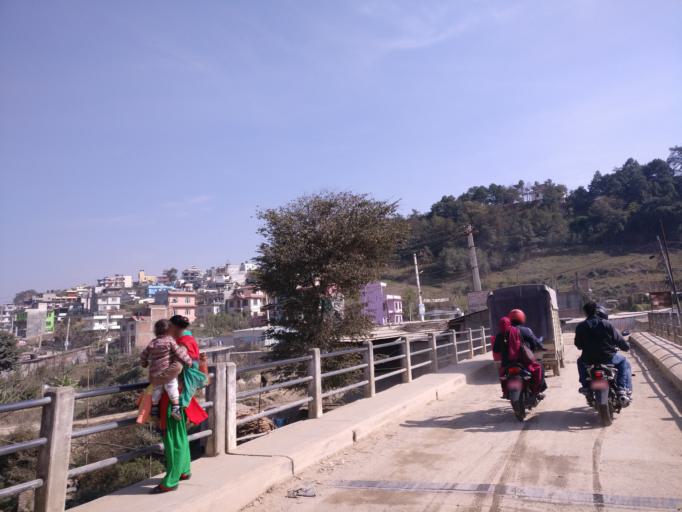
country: NP
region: Central Region
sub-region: Bagmati Zone
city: Patan
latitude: 27.6502
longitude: 85.3121
